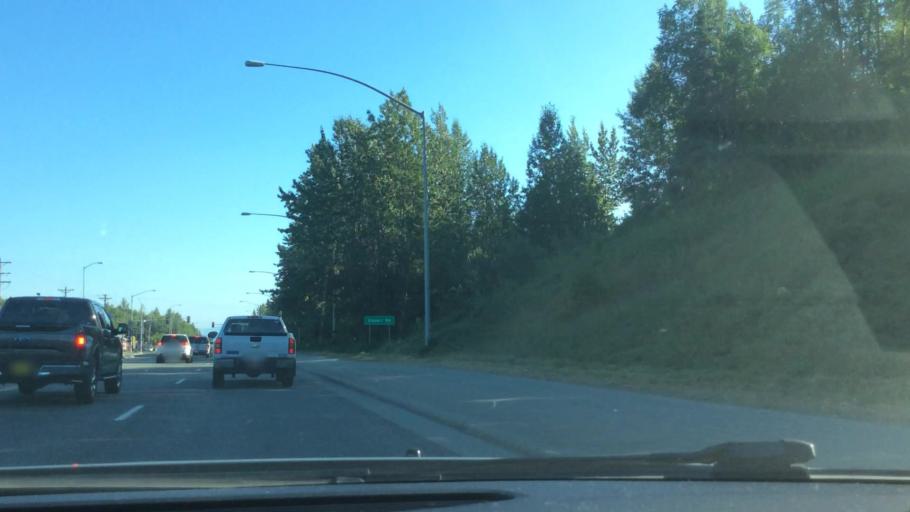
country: US
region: Alaska
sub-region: Anchorage Municipality
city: Anchorage
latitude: 61.2116
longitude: -149.7786
